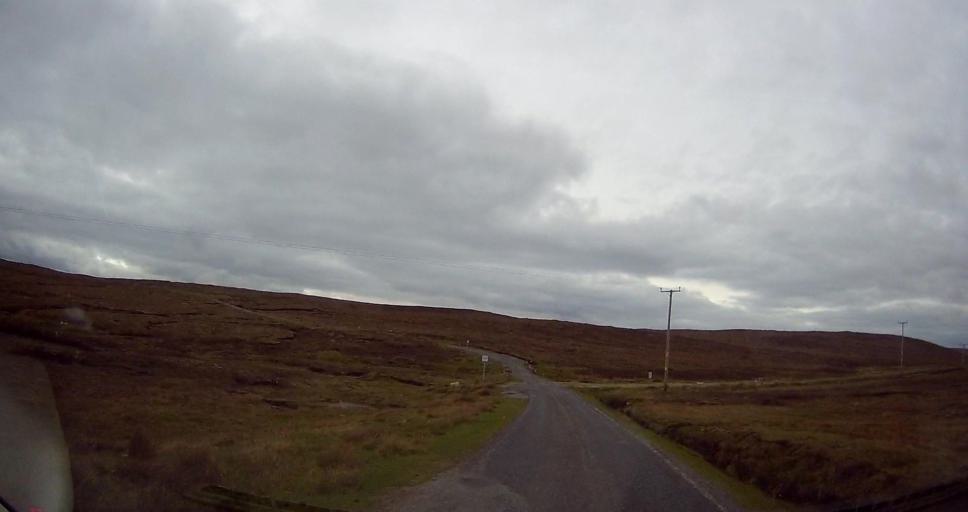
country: GB
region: Scotland
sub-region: Shetland Islands
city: Shetland
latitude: 60.5111
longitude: -1.1163
